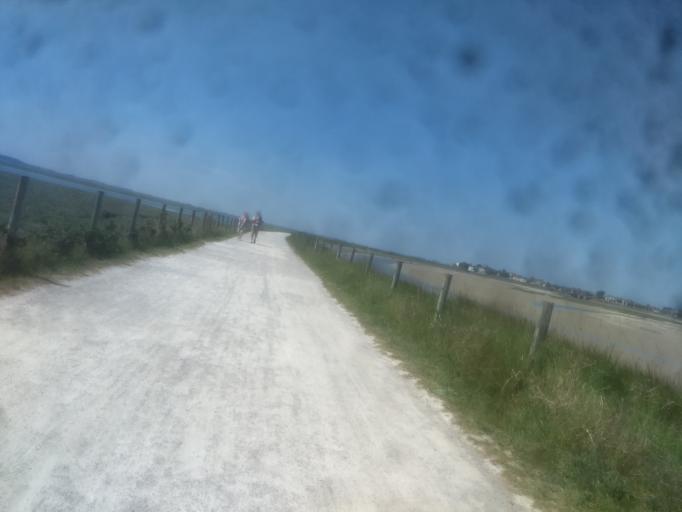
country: FR
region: Picardie
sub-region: Departement de la Somme
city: Le Crotoy
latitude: 50.2134
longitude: 1.6443
